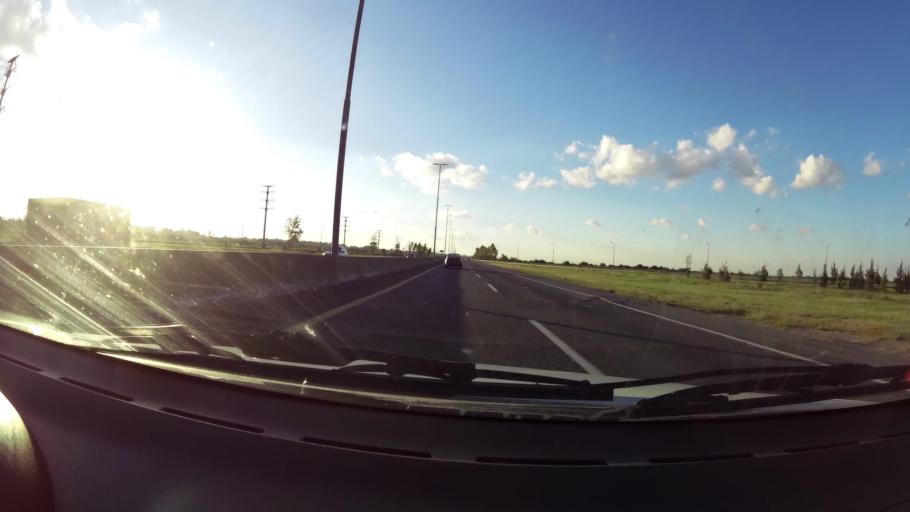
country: AR
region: Buenos Aires
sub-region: Partido de La Plata
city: La Plata
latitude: -34.8389
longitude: -58.0700
